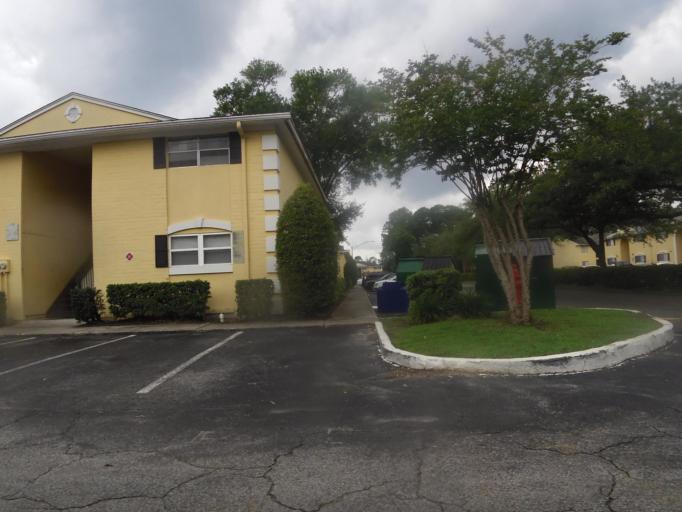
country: US
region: Florida
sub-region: Duval County
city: Jacksonville
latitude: 30.4060
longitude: -81.6625
